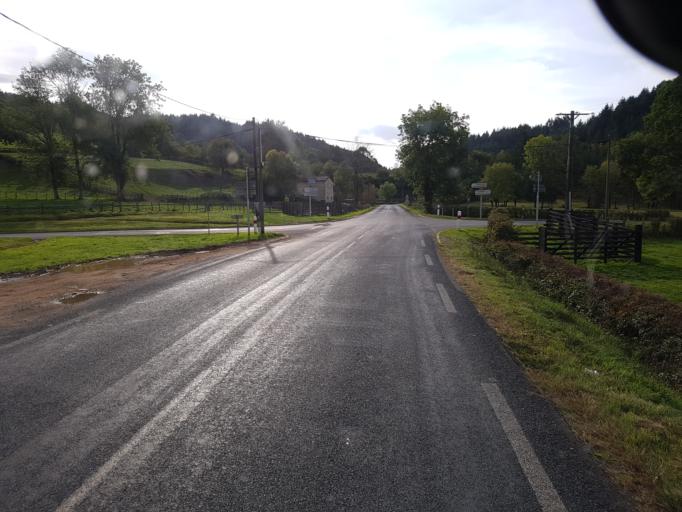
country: FR
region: Bourgogne
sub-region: Departement de Saone-et-Loire
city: Chauffailles
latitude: 46.2395
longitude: 4.4100
